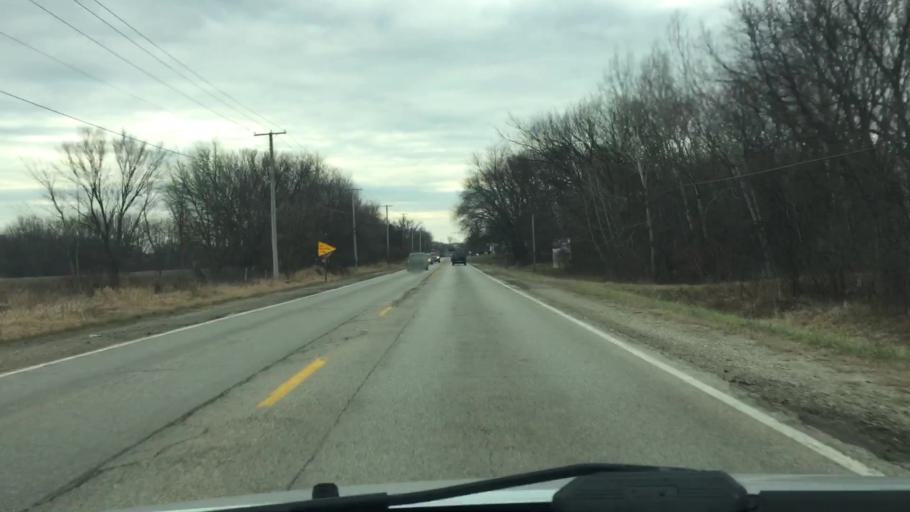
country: US
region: Illinois
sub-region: McHenry County
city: Richmond
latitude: 42.4637
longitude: -88.3066
